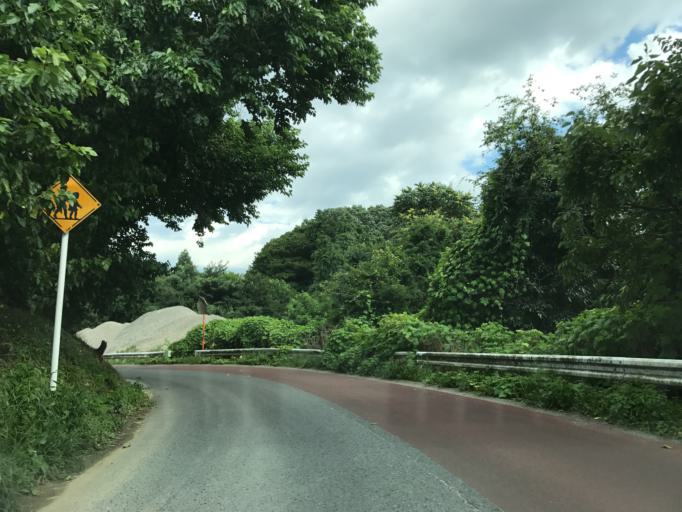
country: JP
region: Fukushima
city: Koriyama
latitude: 37.4089
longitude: 140.4255
